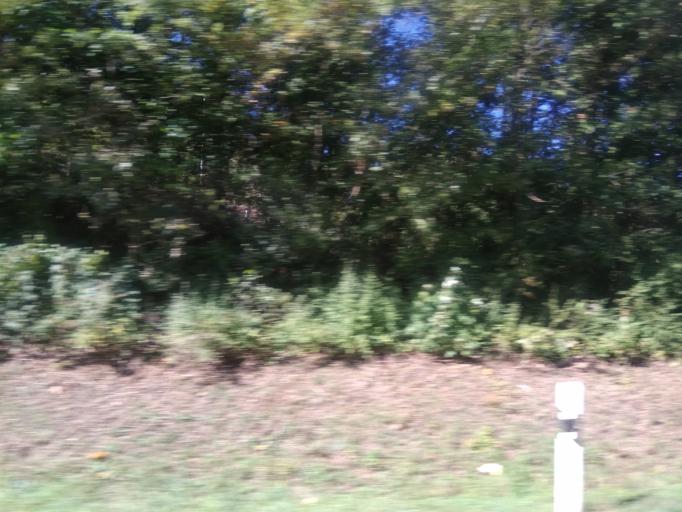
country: DE
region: Baden-Wuerttemberg
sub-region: Karlsruhe Region
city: Billigheim
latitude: 49.3805
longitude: 9.2687
